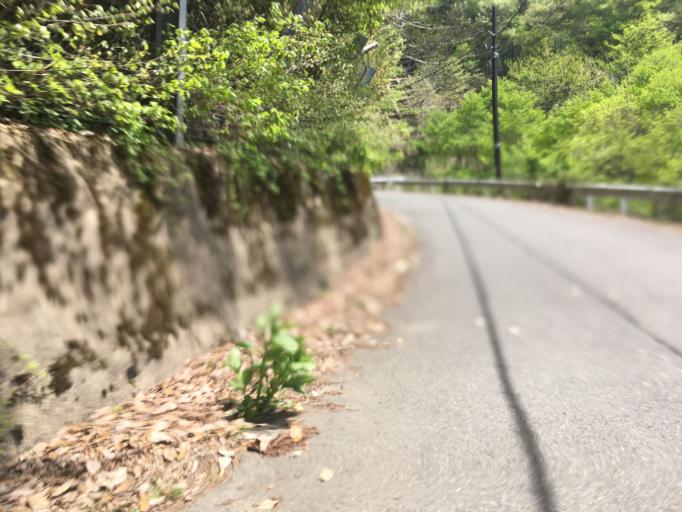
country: JP
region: Kyoto
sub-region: Kyoto-shi
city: Kamigyo-ku
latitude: 35.1143
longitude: 135.7090
